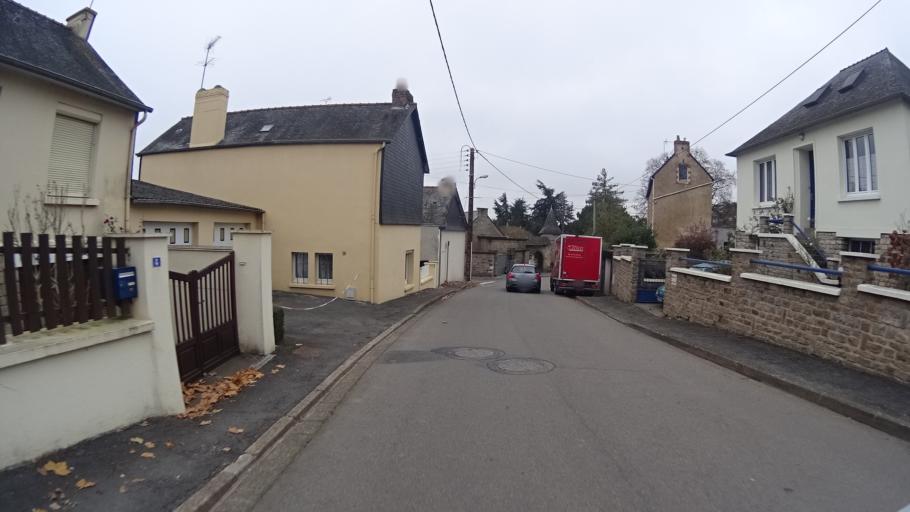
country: FR
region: Brittany
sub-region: Departement d'Ille-et-Vilaine
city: Redon
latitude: 47.6551
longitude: -2.0879
